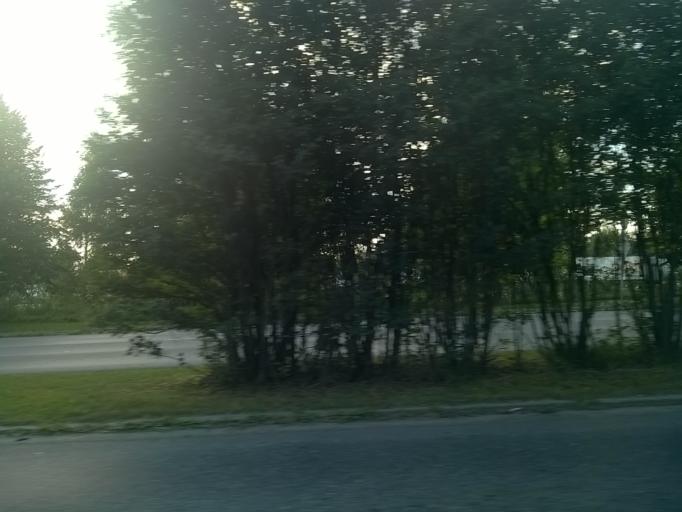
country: FI
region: Pirkanmaa
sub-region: Tampere
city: Tampere
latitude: 61.4874
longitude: 23.7790
